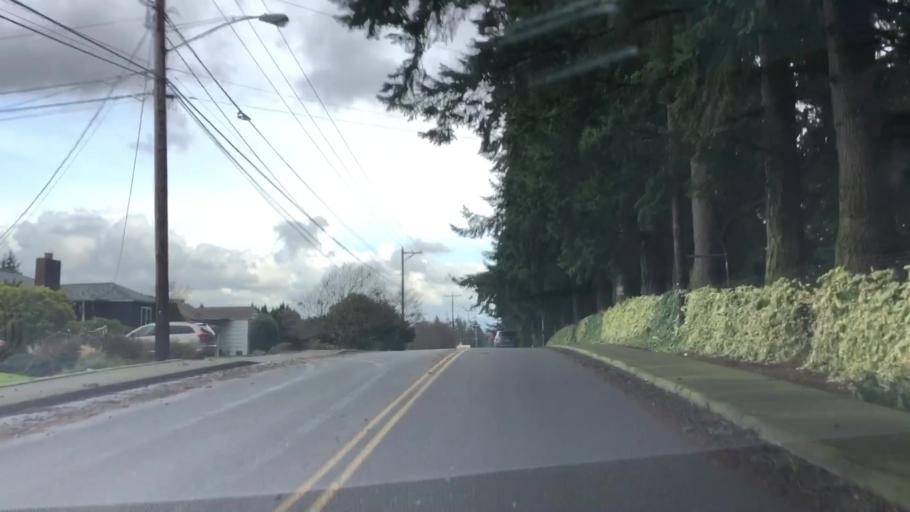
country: US
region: Washington
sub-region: Snohomish County
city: Everett
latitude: 47.9494
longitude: -122.2108
